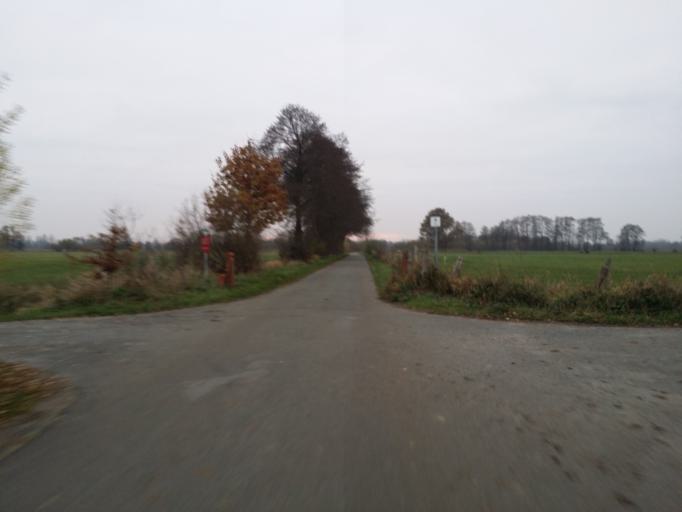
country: DE
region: Lower Saxony
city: Grasberg
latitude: 53.1134
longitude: 8.9853
